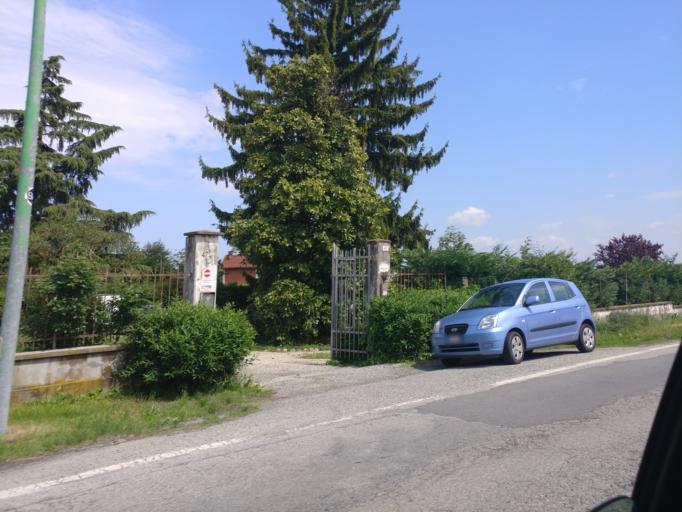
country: IT
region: Piedmont
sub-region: Provincia di Torino
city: Cavour
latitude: 44.7817
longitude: 7.3828
